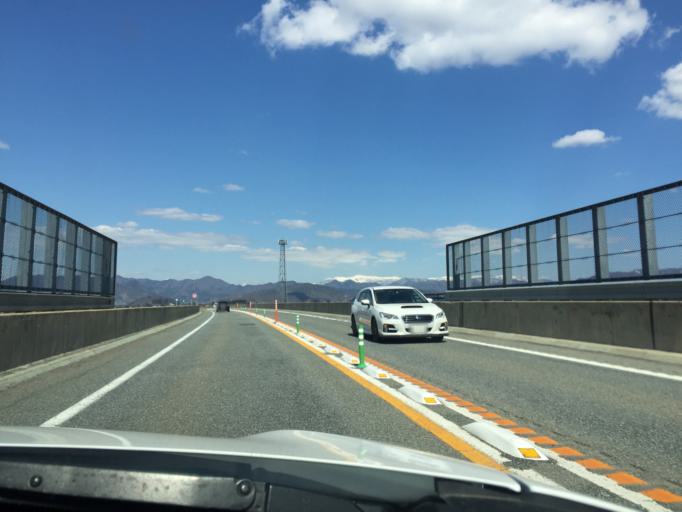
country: JP
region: Yamagata
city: Takahata
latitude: 37.9852
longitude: 140.1526
